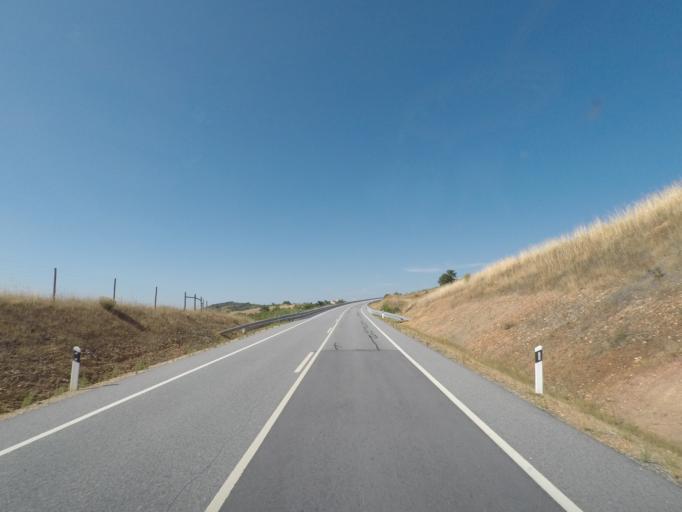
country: PT
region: Braganca
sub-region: Mogadouro
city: Mogadouro
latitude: 41.3452
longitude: -6.6240
